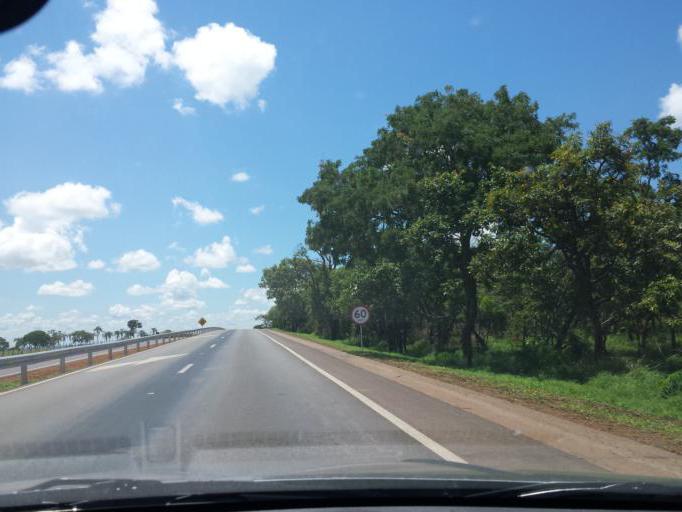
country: BR
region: Goias
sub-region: Luziania
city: Luziania
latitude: -16.3603
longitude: -47.8305
